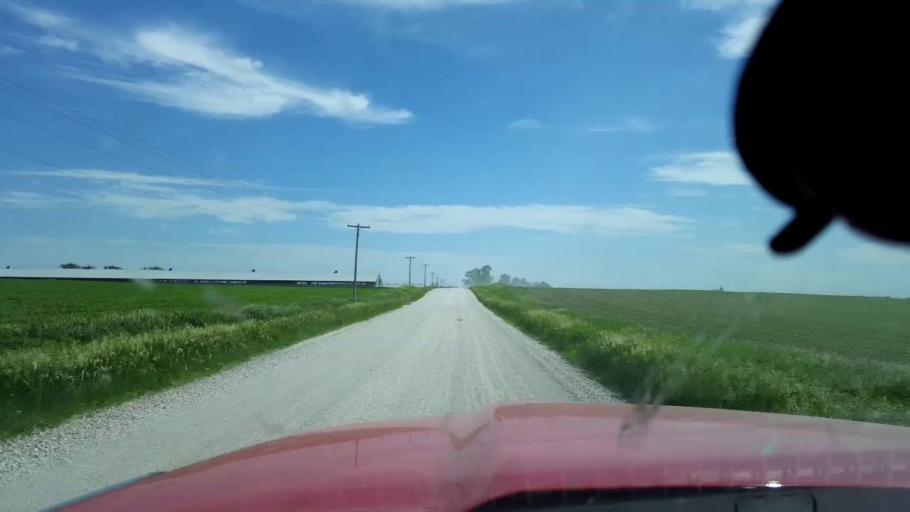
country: US
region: Iowa
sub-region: Hamilton County
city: Jewell
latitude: 42.3450
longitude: -93.5603
